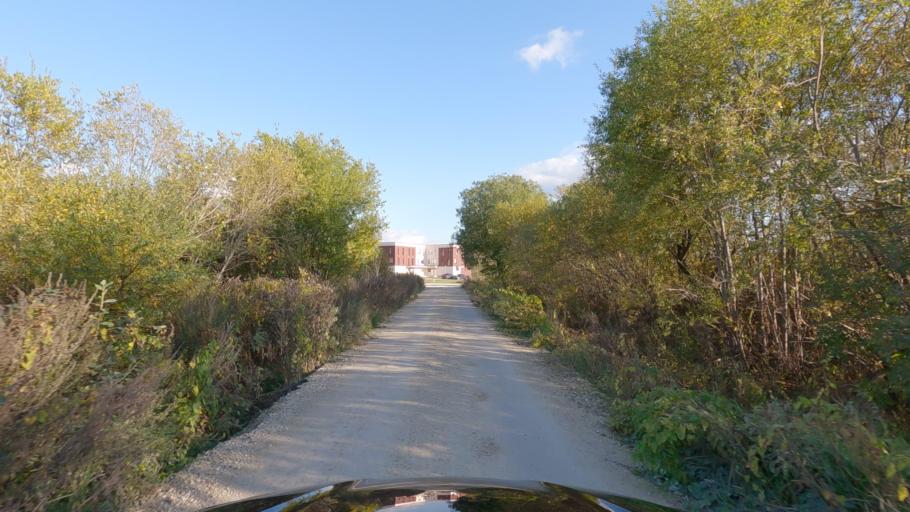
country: EE
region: Harju
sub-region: Saue vald
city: Laagri
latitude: 59.3483
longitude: 24.6458
